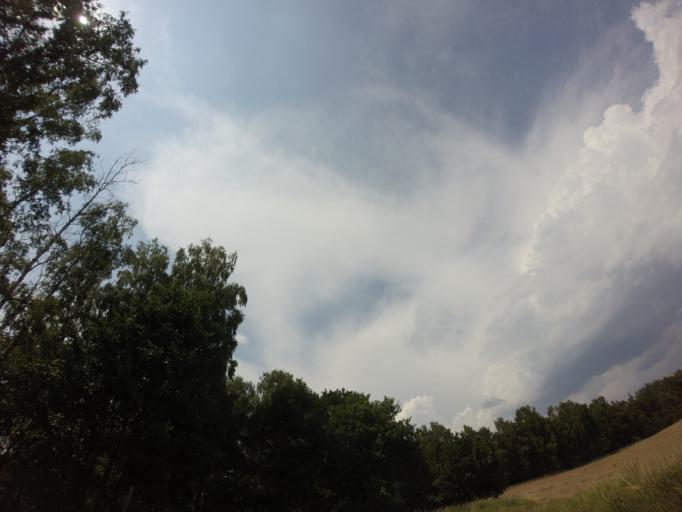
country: PL
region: West Pomeranian Voivodeship
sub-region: Powiat choszczenski
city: Bierzwnik
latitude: 53.1221
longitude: 15.5976
